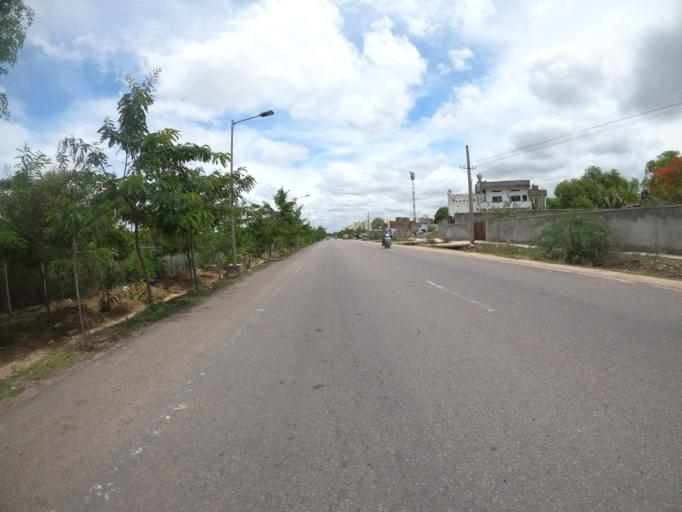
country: IN
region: Telangana
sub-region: Hyderabad
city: Hyderabad
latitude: 17.3324
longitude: 78.3707
